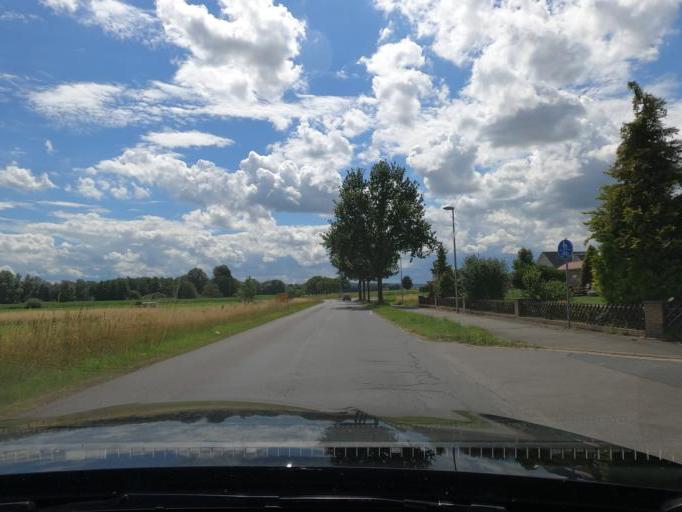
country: DE
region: Lower Saxony
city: Lengede
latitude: 52.1719
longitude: 10.3083
